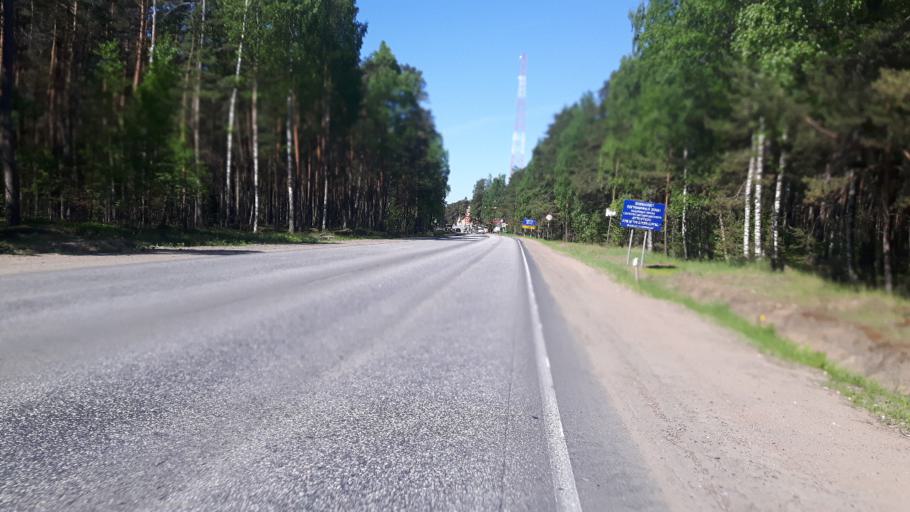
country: RU
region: Leningrad
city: Lebyazh'ye
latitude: 59.9574
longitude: 29.4546
